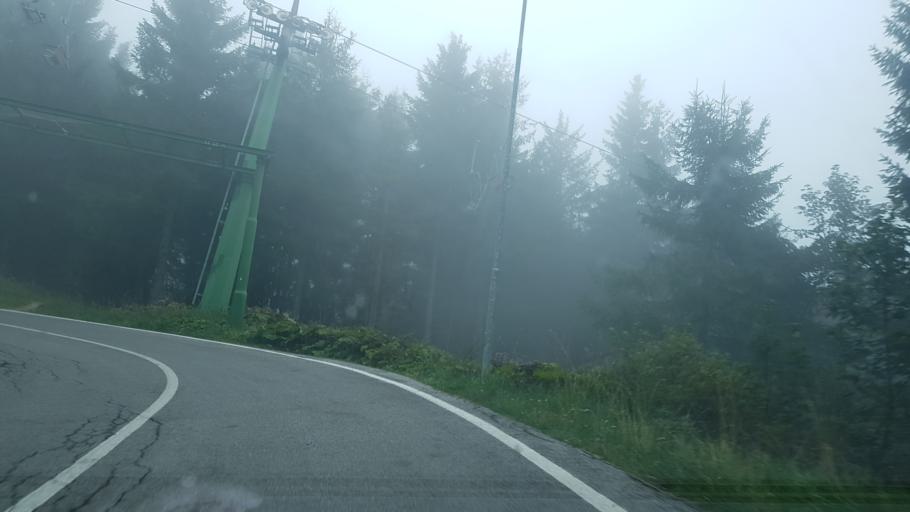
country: IT
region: Piedmont
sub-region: Provincia di Cuneo
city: Frabosa Soprana
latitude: 44.2565
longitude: 7.7933
